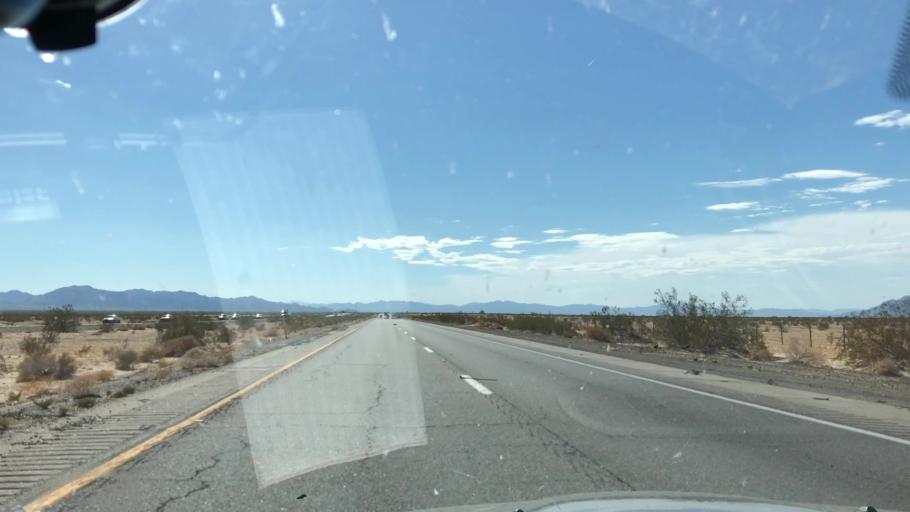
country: US
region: California
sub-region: Riverside County
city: Mesa Verde
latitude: 33.6420
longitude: -115.1048
